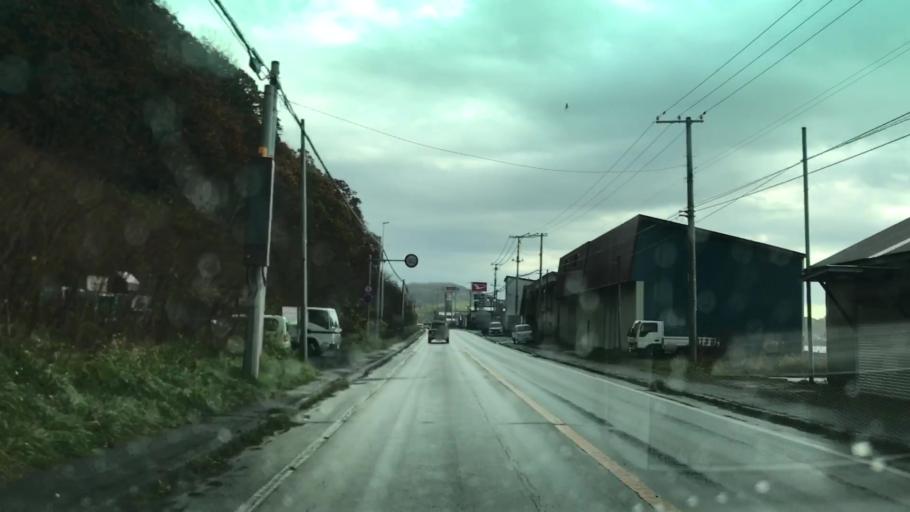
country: JP
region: Hokkaido
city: Shizunai-furukawacho
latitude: 42.1770
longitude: 142.7513
